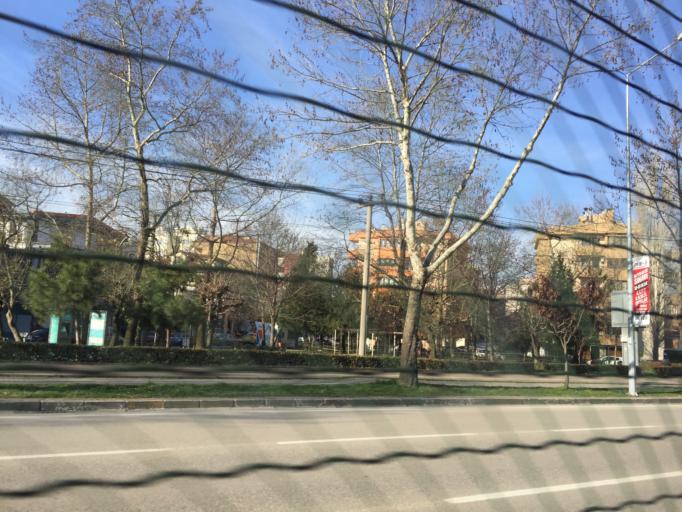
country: TR
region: Bursa
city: Yildirim
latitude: 40.2227
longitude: 28.9942
